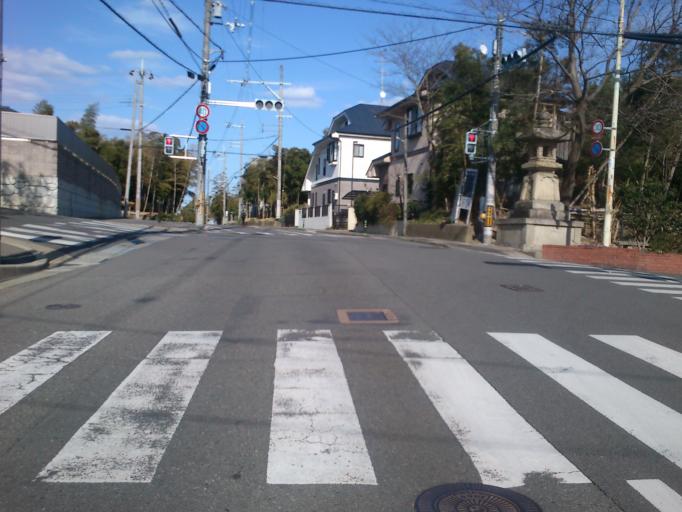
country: JP
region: Kyoto
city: Muko
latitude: 34.9220
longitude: 135.6820
